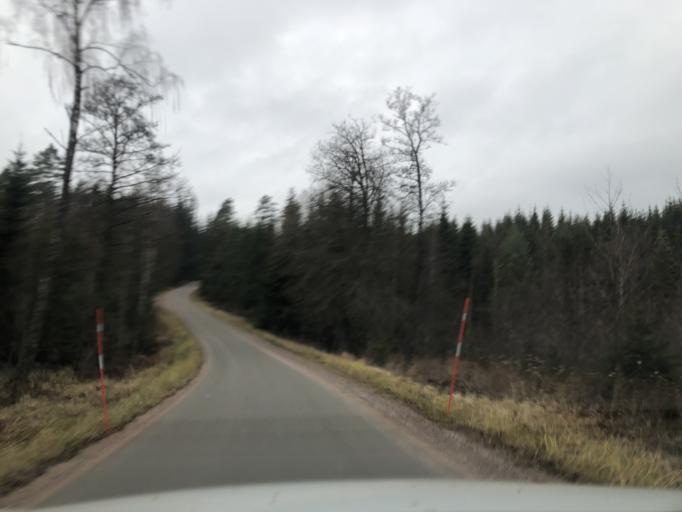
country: SE
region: Vaestra Goetaland
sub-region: Ulricehamns Kommun
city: Ulricehamn
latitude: 57.8535
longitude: 13.6314
